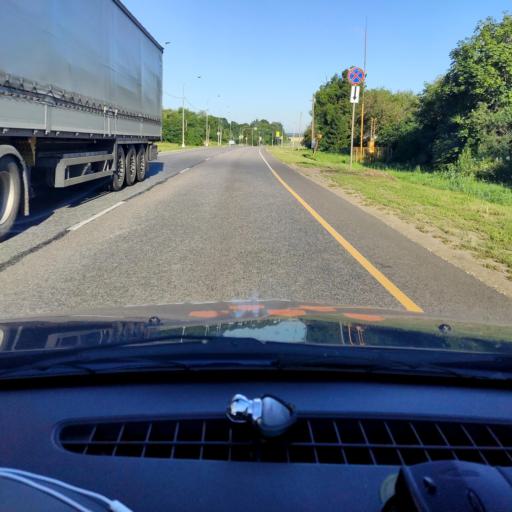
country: RU
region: Orjol
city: Pokrovskoye
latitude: 52.6195
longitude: 36.7436
